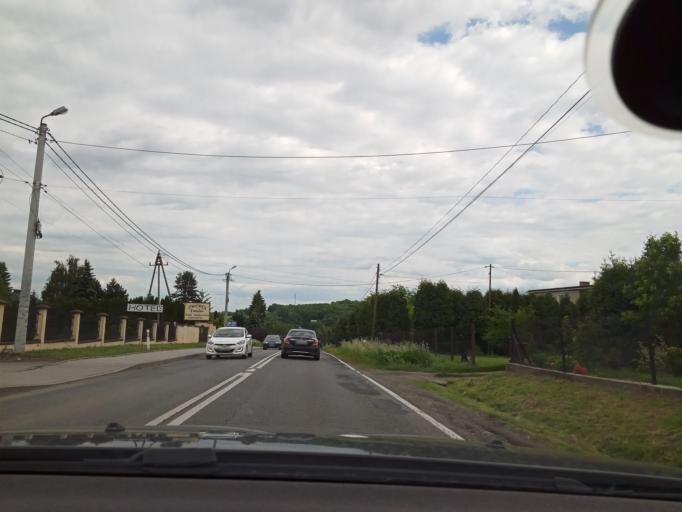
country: PL
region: Lesser Poland Voivodeship
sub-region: Powiat wielicki
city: Tomaszkowice
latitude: 49.9758
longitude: 20.0999
